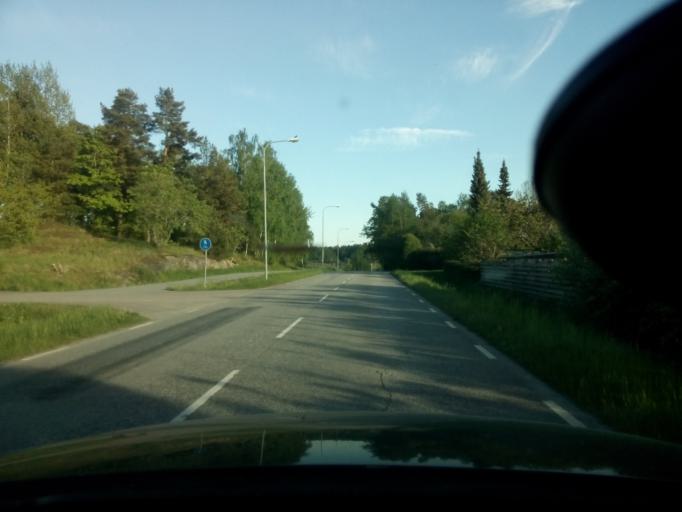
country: SE
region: Soedermanland
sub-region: Nykopings Kommun
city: Nykoping
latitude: 58.7762
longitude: 17.0042
